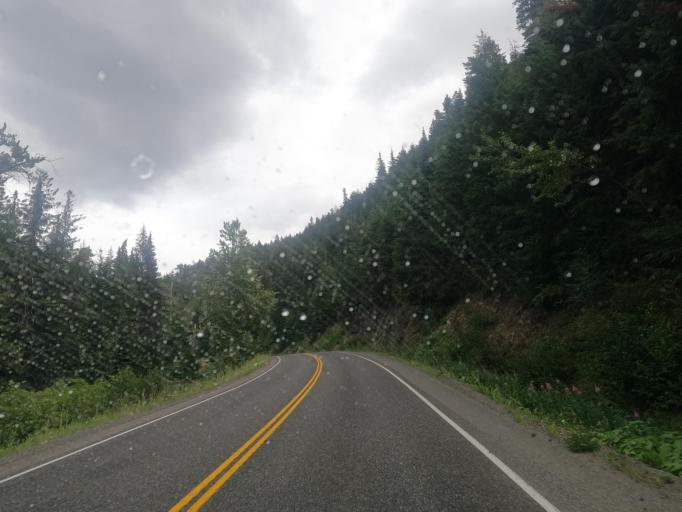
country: CA
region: British Columbia
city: Lillooet
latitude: 50.4783
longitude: -122.2174
